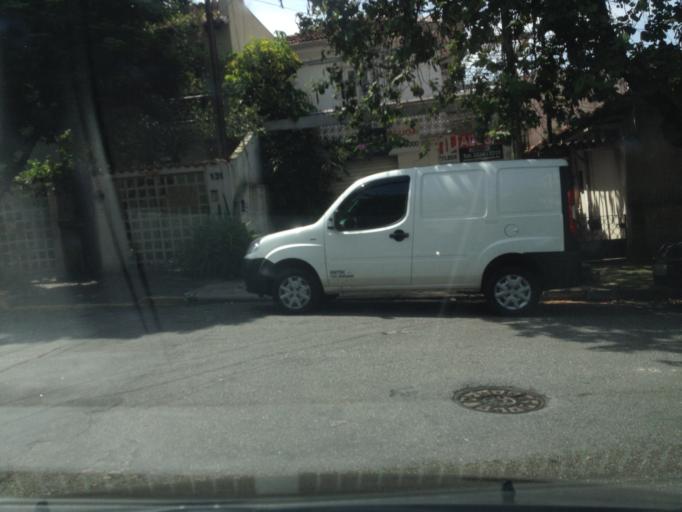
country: BR
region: Sao Paulo
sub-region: Sao Paulo
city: Sao Paulo
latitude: -23.5531
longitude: -46.6882
